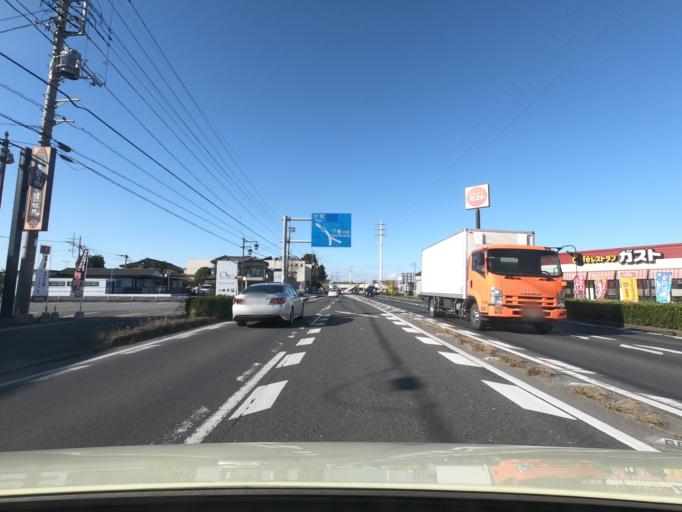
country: JP
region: Ibaraki
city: Ishige
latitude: 36.1824
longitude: 139.9505
